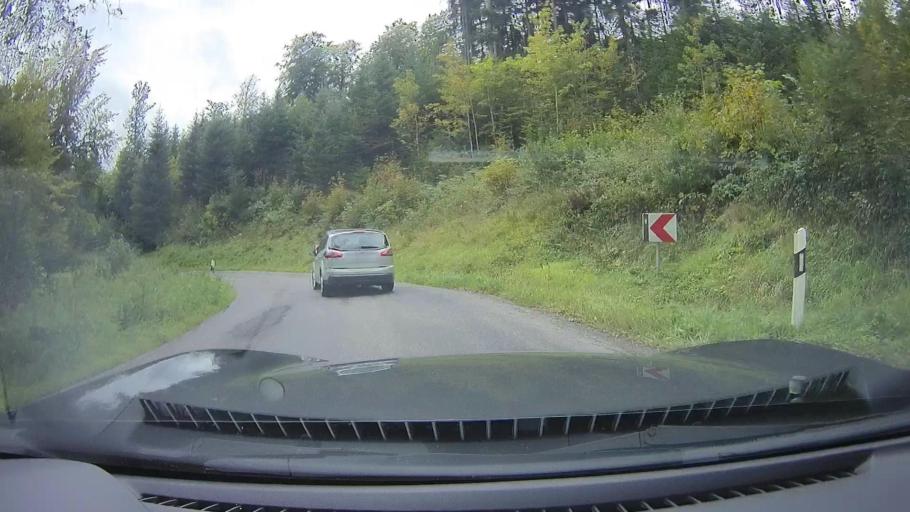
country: DE
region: Baden-Wuerttemberg
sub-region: Regierungsbezirk Stuttgart
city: Murrhardt
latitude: 48.9896
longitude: 9.5805
